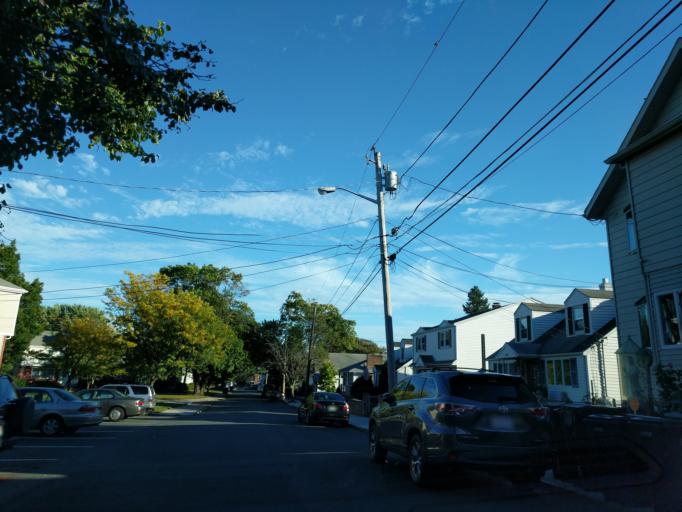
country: US
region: Massachusetts
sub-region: Middlesex County
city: Everett
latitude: 42.4136
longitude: -71.0351
